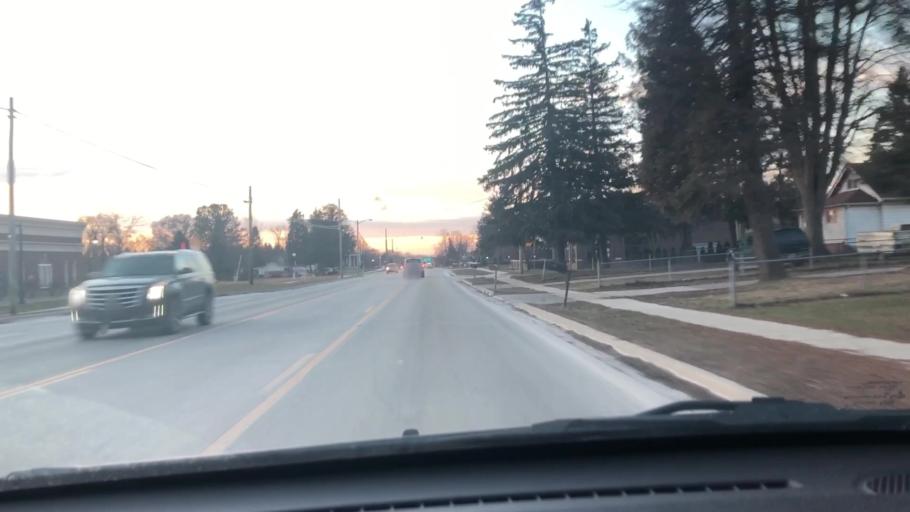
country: US
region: Michigan
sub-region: Macomb County
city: Shelby
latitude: 42.7198
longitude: -83.0356
